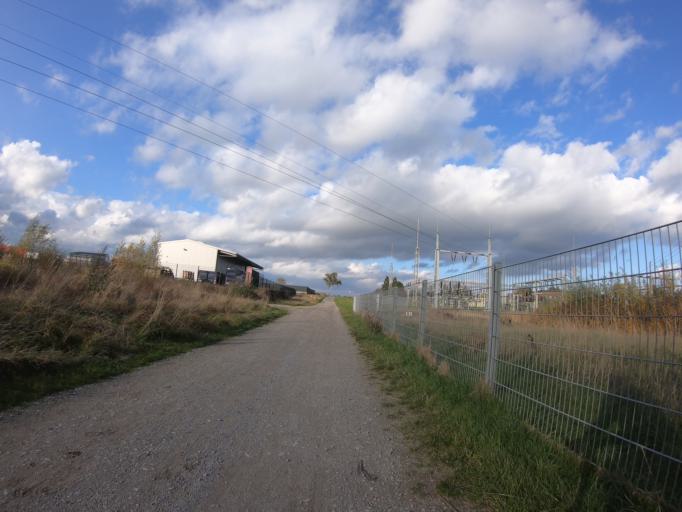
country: DE
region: Lower Saxony
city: Gifhorn
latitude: 52.5060
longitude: 10.5350
